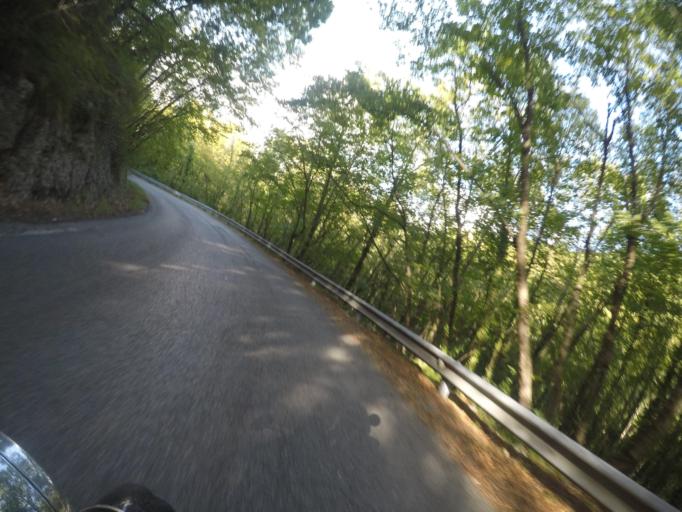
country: IT
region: Tuscany
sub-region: Provincia di Massa-Carrara
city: Massa
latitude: 44.0749
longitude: 10.1181
